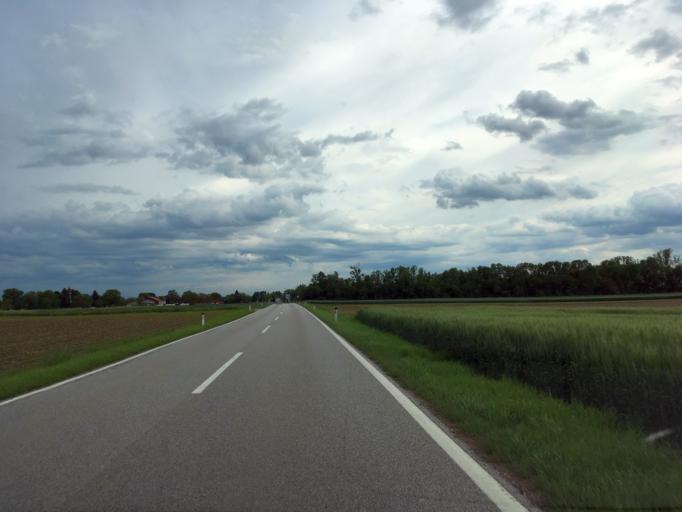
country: AT
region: Lower Austria
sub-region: Politischer Bezirk Tulln
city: Kirchberg am Wagram
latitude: 48.4130
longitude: 15.8907
